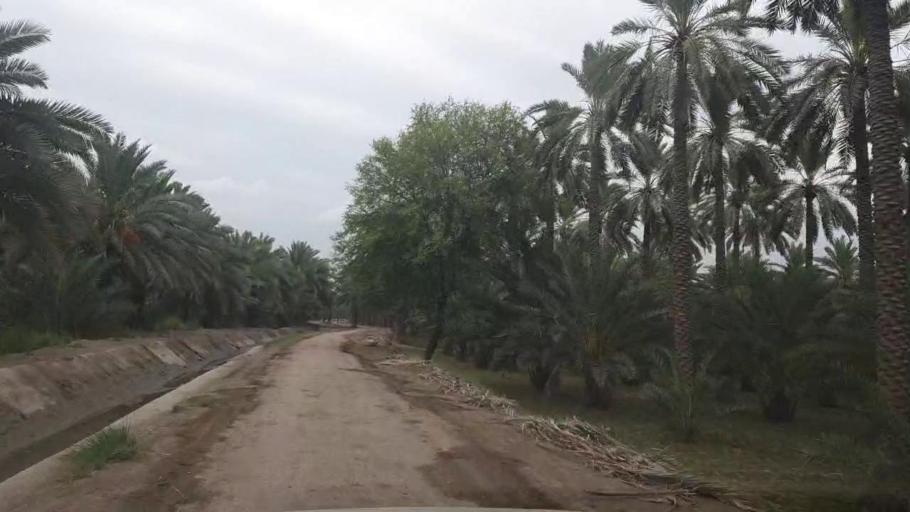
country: PK
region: Sindh
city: Khairpur
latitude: 27.5961
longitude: 68.8007
